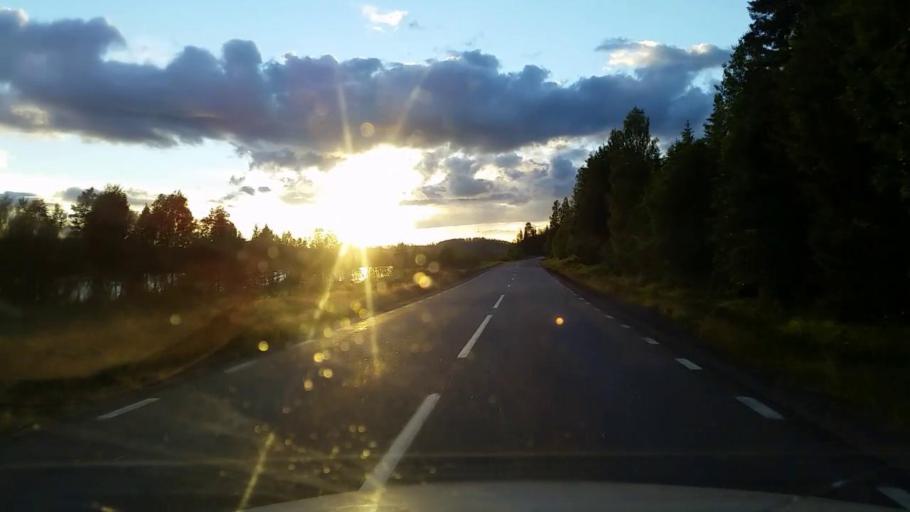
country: SE
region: Gaevleborg
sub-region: Ljusdals Kommun
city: Farila
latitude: 62.1353
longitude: 15.6933
